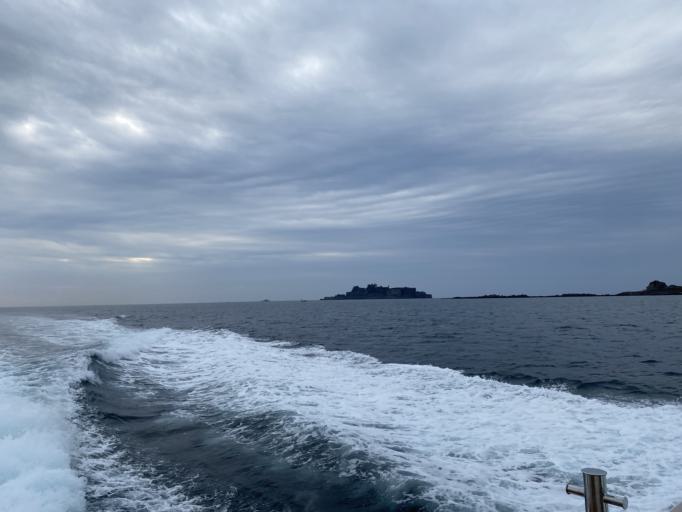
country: JP
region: Nagasaki
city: Nagasaki-shi
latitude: 32.6325
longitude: 129.7564
